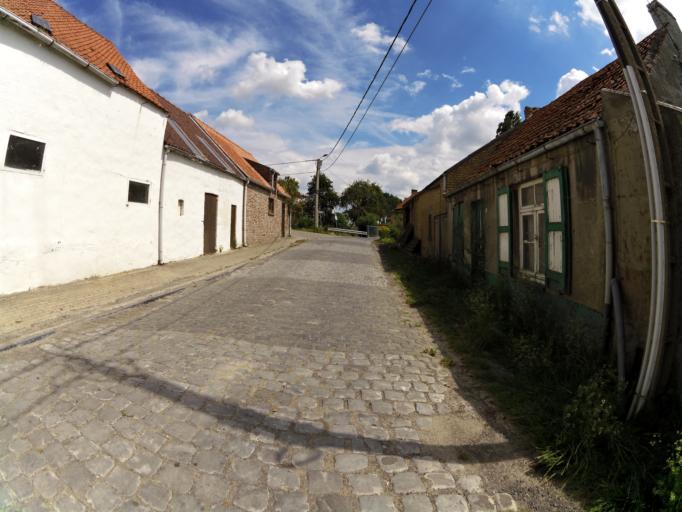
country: BE
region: Flanders
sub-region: Provincie West-Vlaanderen
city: Gistel
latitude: 51.1795
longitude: 2.9402
